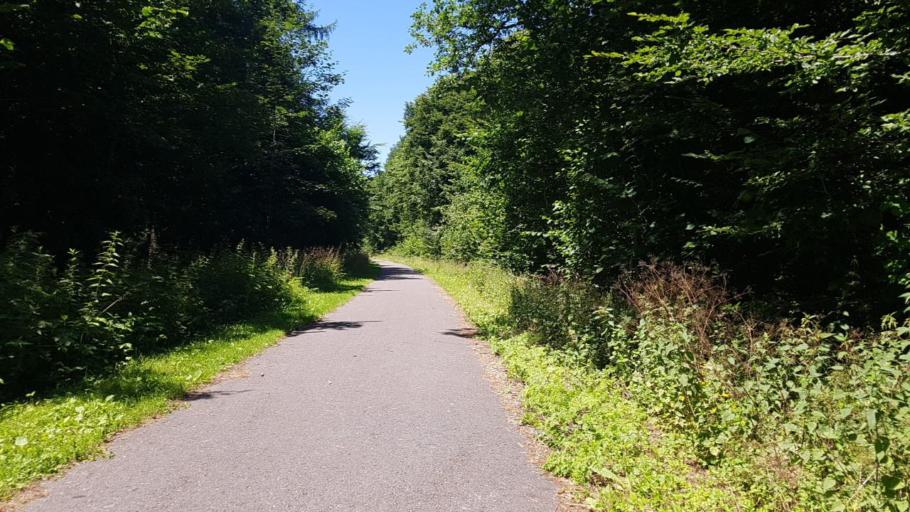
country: BE
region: Wallonia
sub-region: Province du Hainaut
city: Froidchapelle
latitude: 50.1546
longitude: 4.2694
